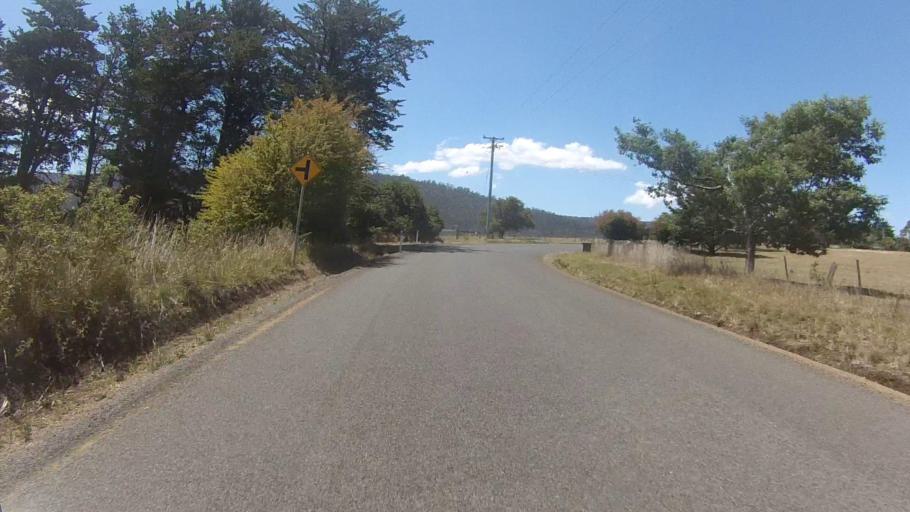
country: AU
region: Tasmania
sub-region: Sorell
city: Sorell
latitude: -42.7607
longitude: 147.6204
